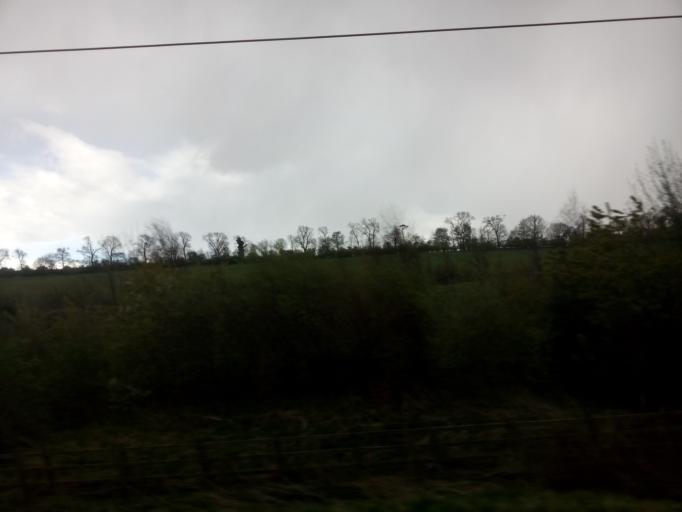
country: GB
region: Scotland
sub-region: East Lothian
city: East Linton
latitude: 55.9860
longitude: -2.6387
